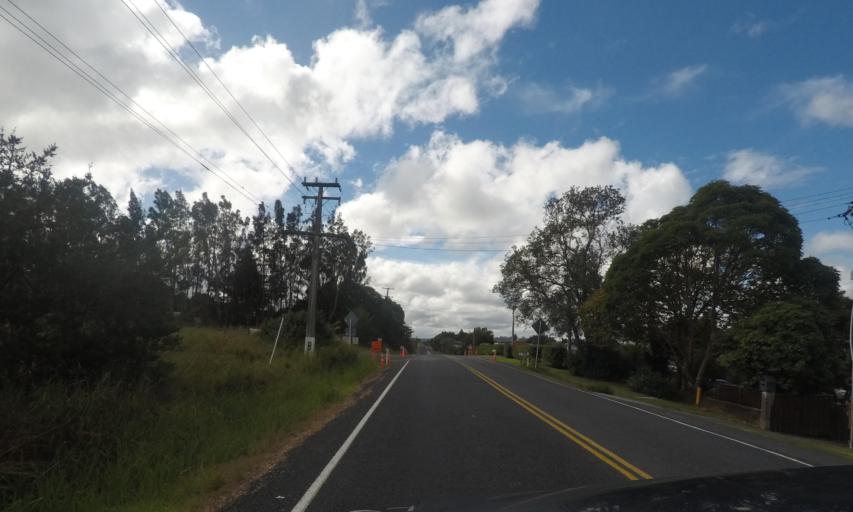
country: NZ
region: Auckland
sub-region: Auckland
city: Rosebank
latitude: -36.7963
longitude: 174.6365
